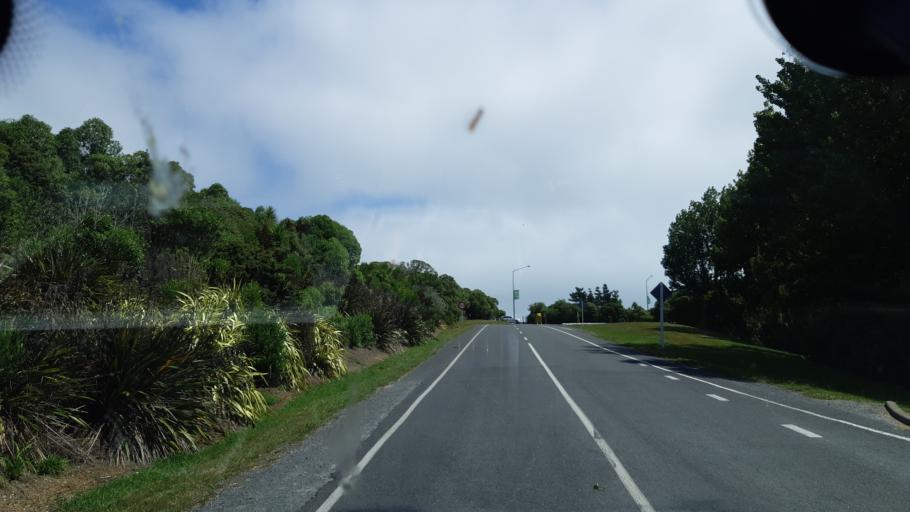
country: NZ
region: Canterbury
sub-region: Kaikoura District
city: Kaikoura
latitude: -42.4089
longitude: 173.6801
